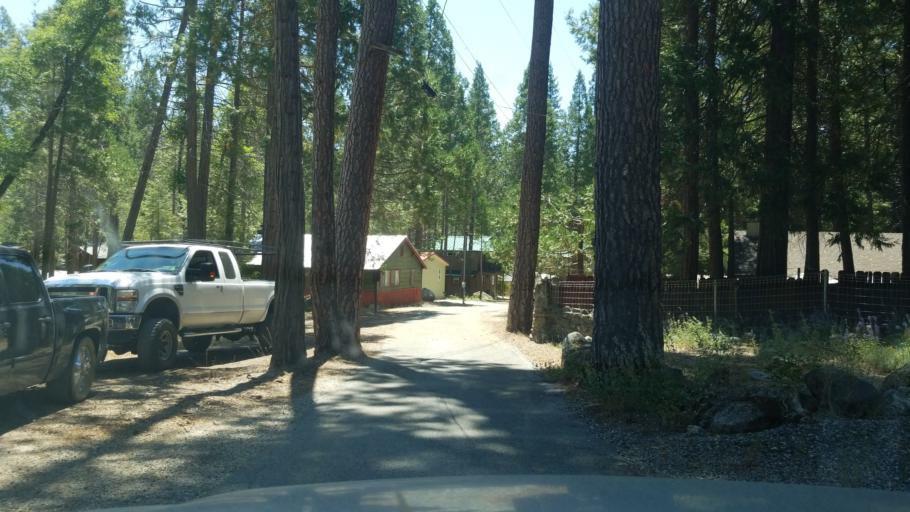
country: US
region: California
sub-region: Madera County
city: Ahwahnee
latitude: 37.5488
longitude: -119.6461
